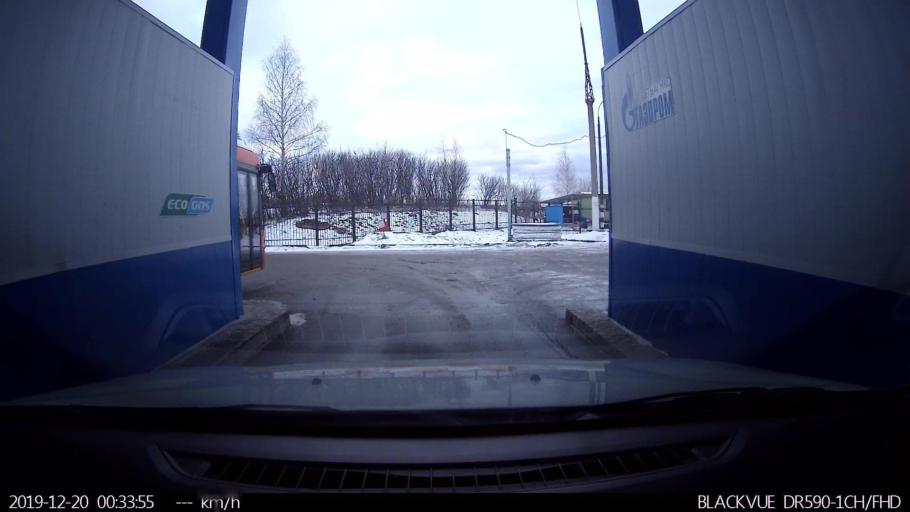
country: RU
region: Vladimir
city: Yur'yev-Pol'skiy
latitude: 56.4626
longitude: 39.6970
